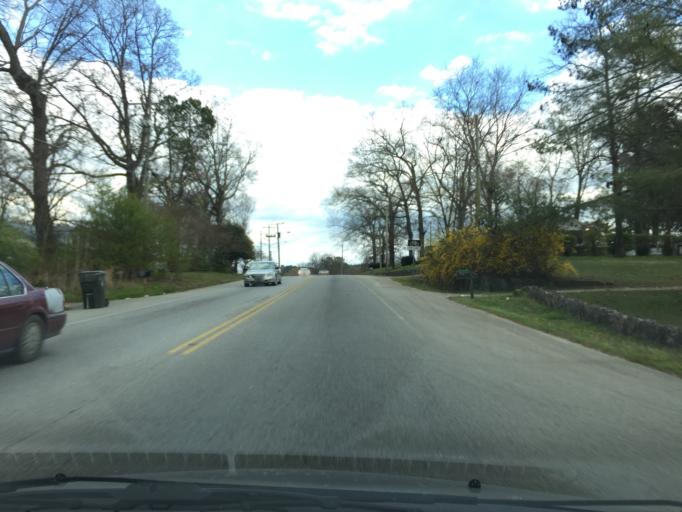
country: US
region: Tennessee
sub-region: Hamilton County
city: East Chattanooga
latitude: 35.0796
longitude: -85.2244
